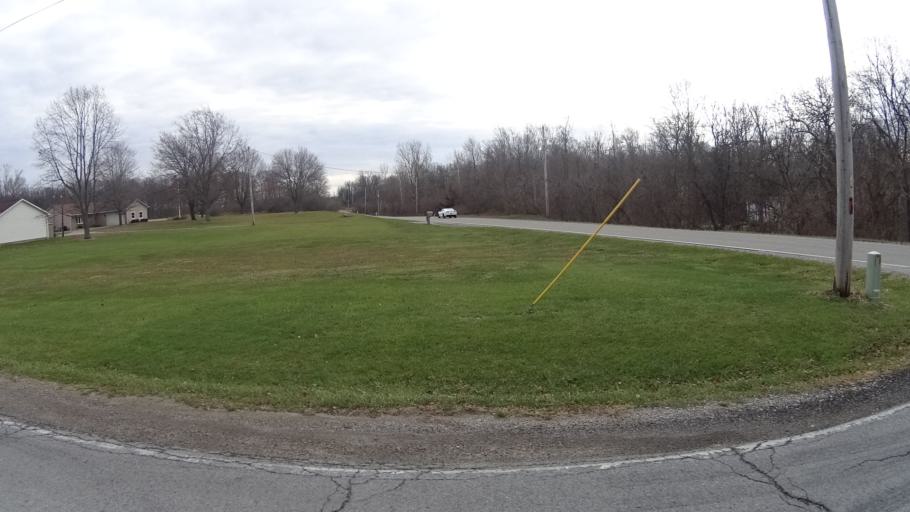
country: US
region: Ohio
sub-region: Lorain County
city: Camden
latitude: 41.1969
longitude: -82.3599
